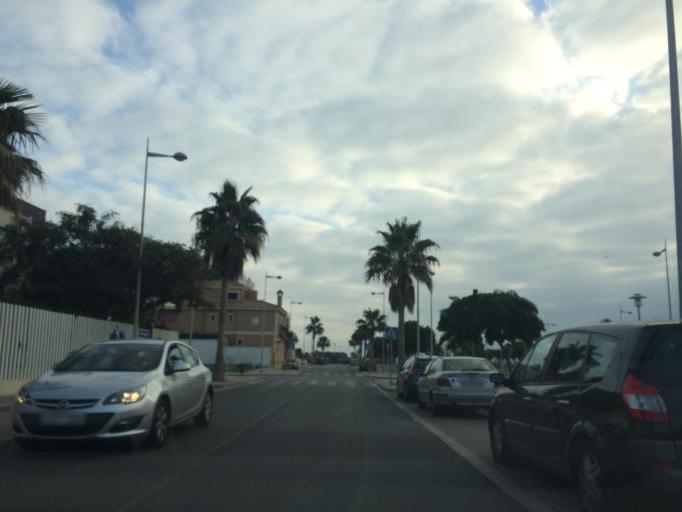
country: ES
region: Andalusia
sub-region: Provincia de Almeria
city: Almeria
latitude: 36.8302
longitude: -2.4403
